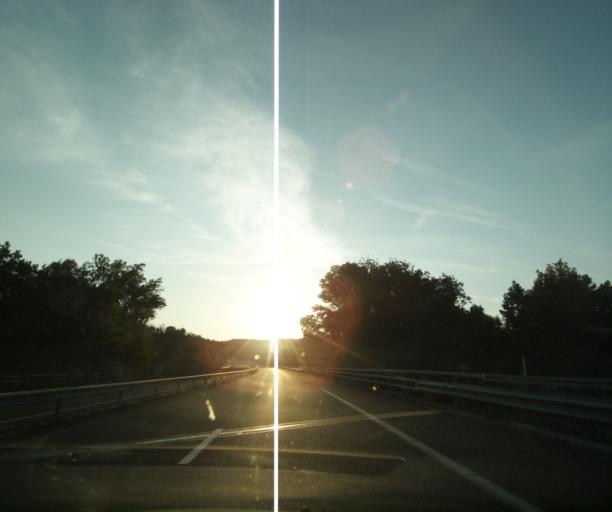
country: FR
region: Aquitaine
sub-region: Departement du Lot-et-Garonne
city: Layrac
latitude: 44.1431
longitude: 0.6556
